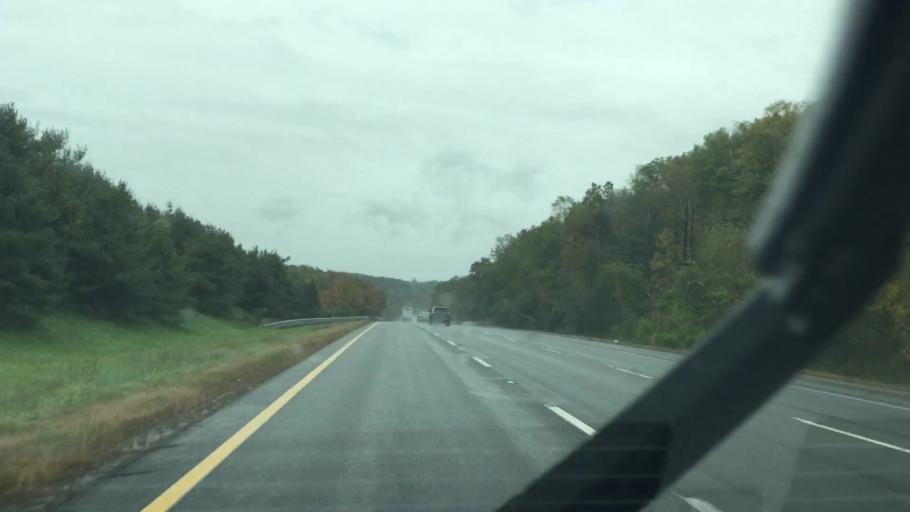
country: US
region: Massachusetts
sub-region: Essex County
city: Merrimac
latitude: 42.8228
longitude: -71.0123
